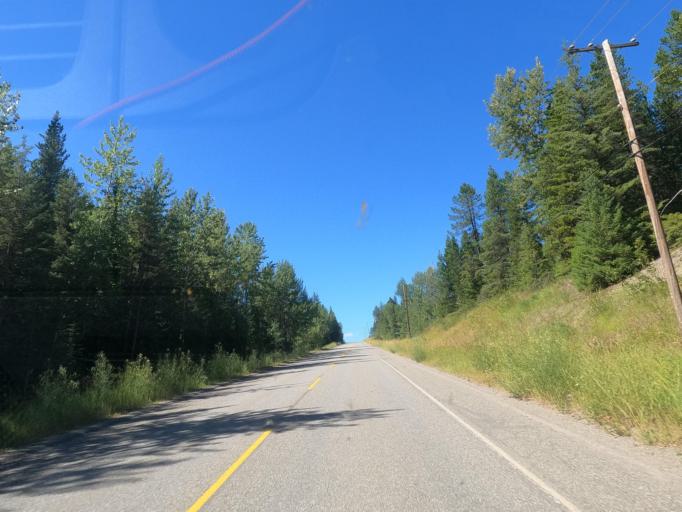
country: CA
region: British Columbia
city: Quesnel
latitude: 53.0303
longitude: -122.4149
